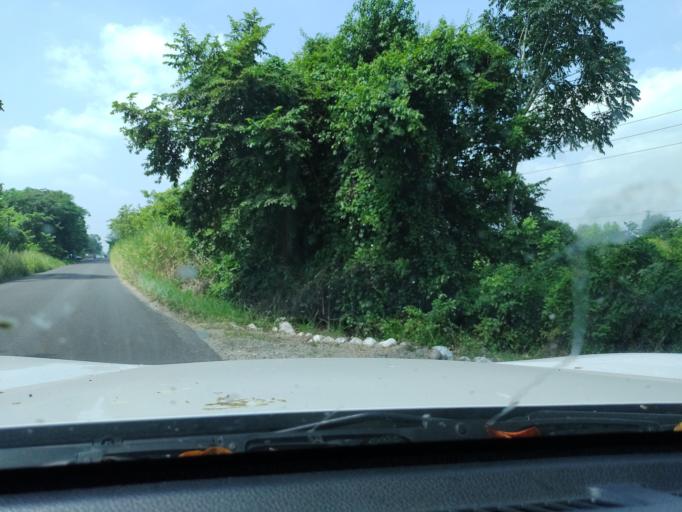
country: MX
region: Veracruz
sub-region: Atzalan
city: Colonias Pedernales
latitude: 20.0587
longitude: -97.0290
